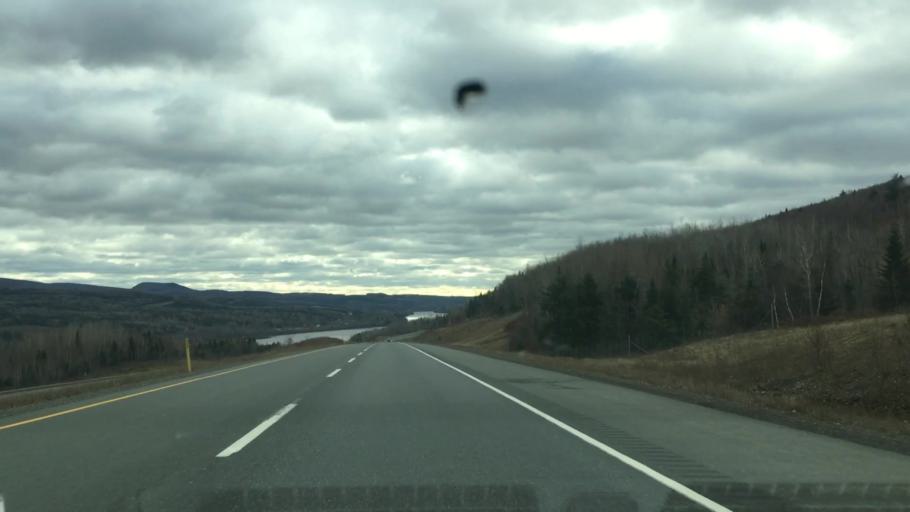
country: US
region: Maine
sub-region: Aroostook County
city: Fort Fairfield
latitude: 46.6909
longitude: -67.7380
